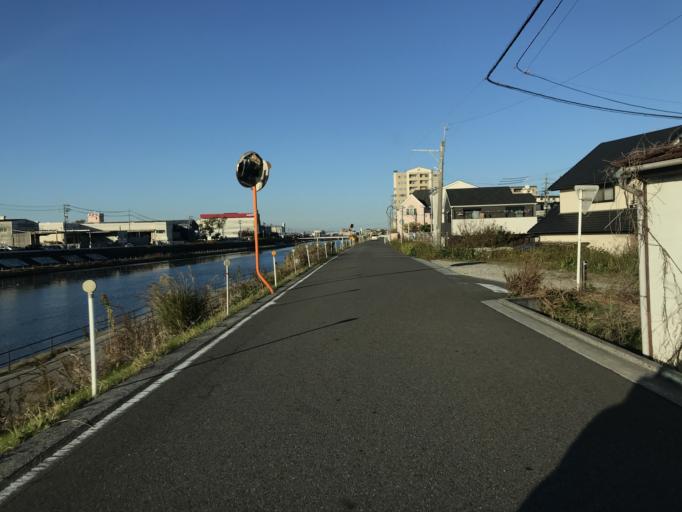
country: JP
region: Aichi
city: Nagoya-shi
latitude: 35.1861
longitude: 136.8467
